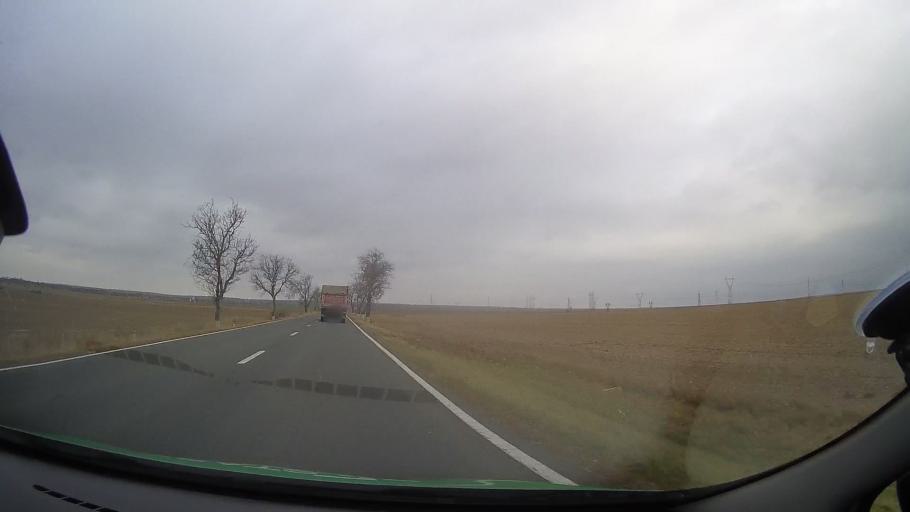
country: RO
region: Constanta
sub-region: Comuna Castelu
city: Castelu
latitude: 44.2502
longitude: 28.3570
